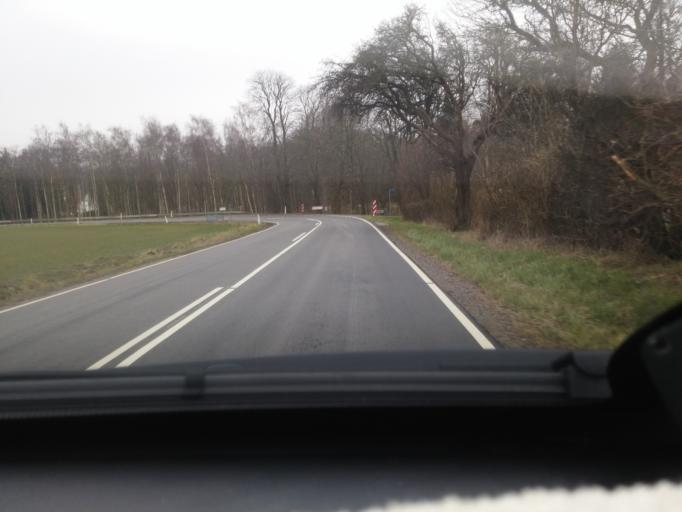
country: DK
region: South Denmark
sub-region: Kerteminde Kommune
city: Kerteminde
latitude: 55.4123
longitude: 10.7106
